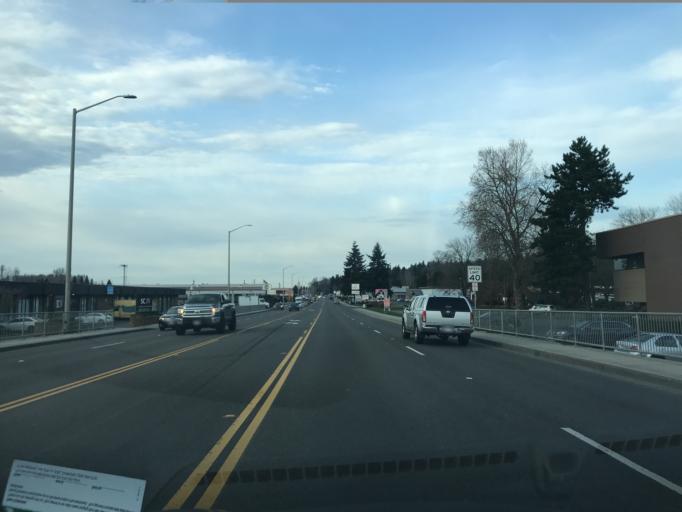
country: US
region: Washington
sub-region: King County
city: Kent
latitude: 47.3620
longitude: -122.2299
